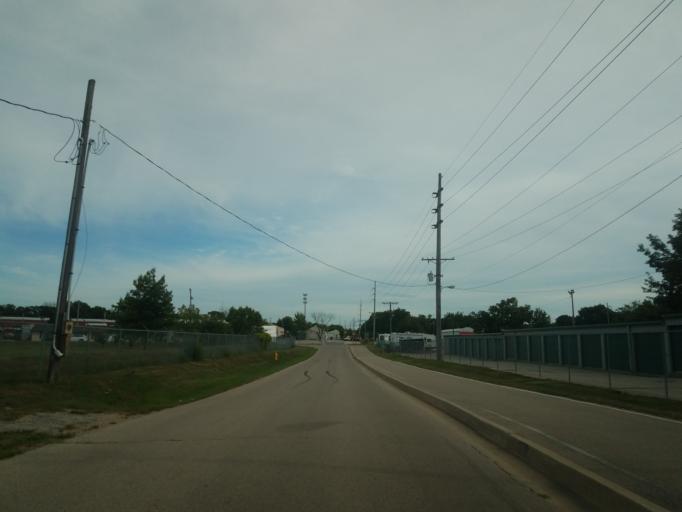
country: US
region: Illinois
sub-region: McLean County
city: Bloomington
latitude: 40.4703
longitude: -88.9808
